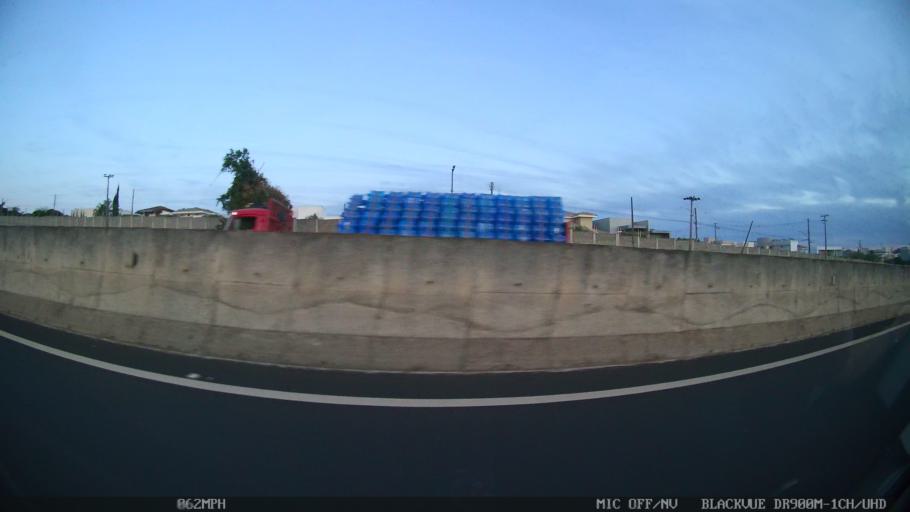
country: BR
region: Sao Paulo
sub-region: Catanduva
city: Catanduva
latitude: -21.1168
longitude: -48.9811
